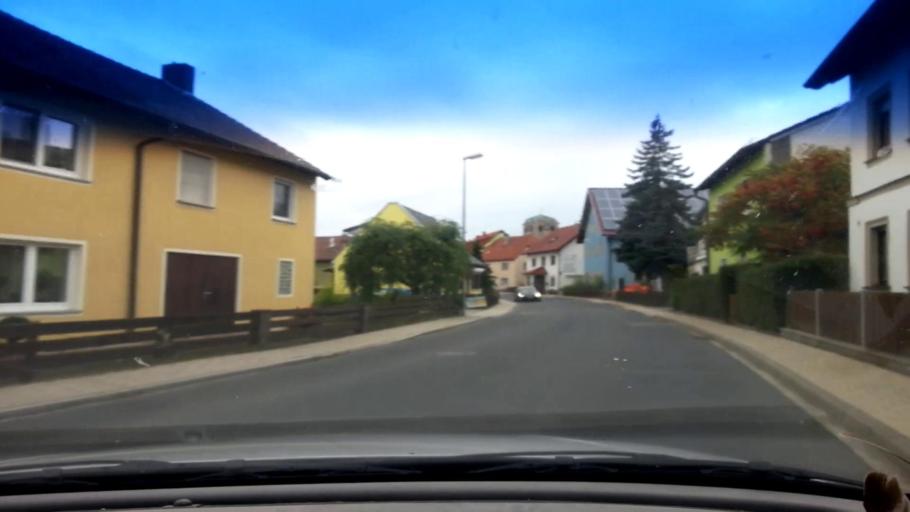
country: DE
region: Bavaria
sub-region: Upper Franconia
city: Priesendorf
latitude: 49.9058
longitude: 10.7137
